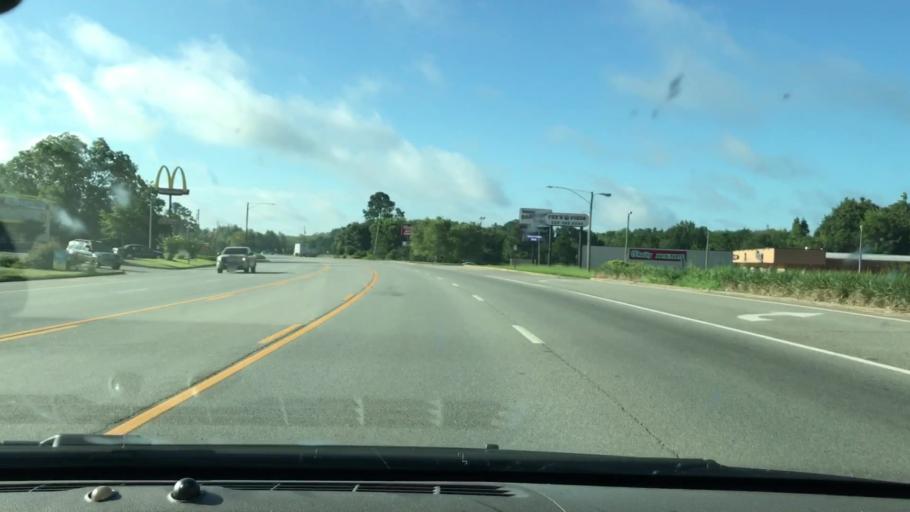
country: US
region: Georgia
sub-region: Terrell County
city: Dawson
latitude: 31.7694
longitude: -84.4482
